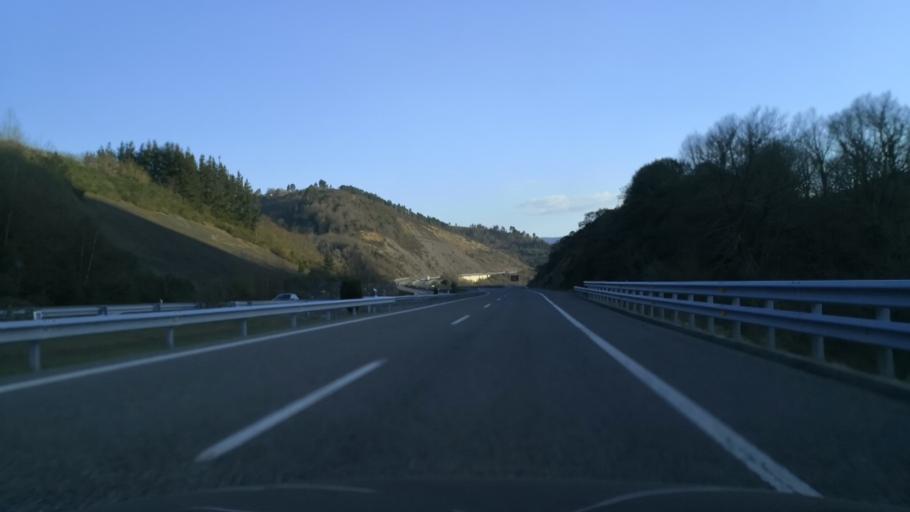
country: ES
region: Galicia
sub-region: Provincia de Lugo
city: Becerrea
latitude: 42.8452
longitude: -7.1205
